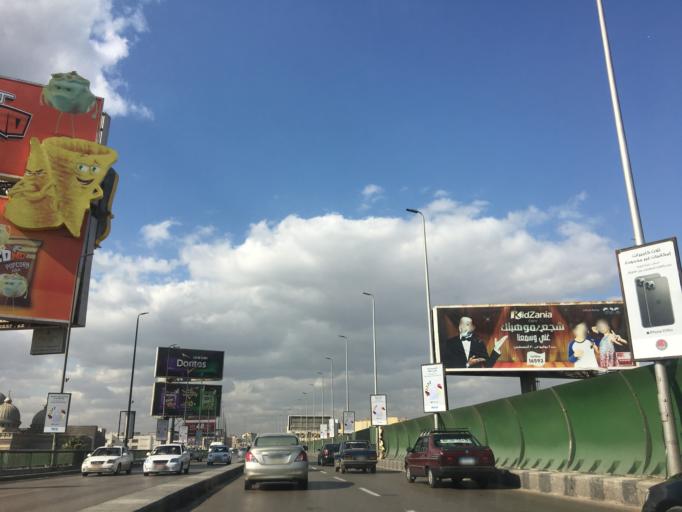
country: EG
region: Muhafazat al Qahirah
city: Cairo
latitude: 30.0745
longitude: 31.2858
